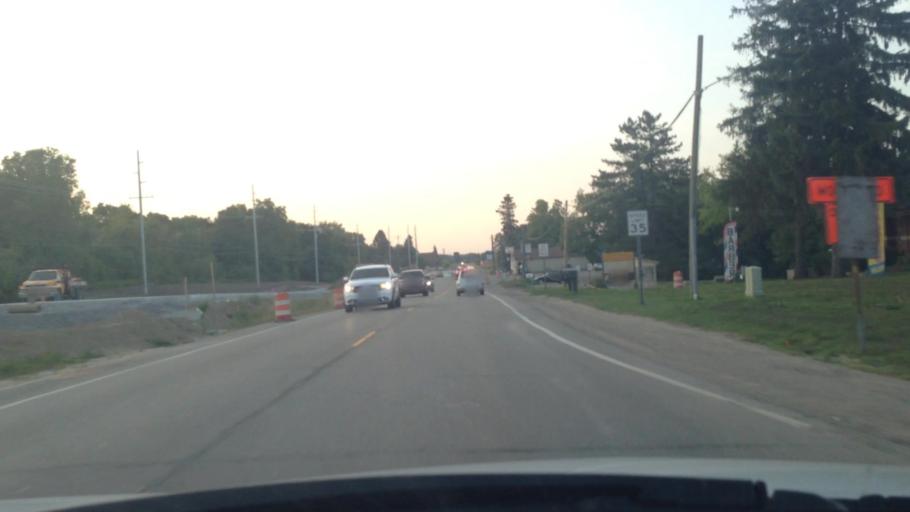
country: US
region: Michigan
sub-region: Oakland County
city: Pontiac
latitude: 42.7153
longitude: -83.3072
